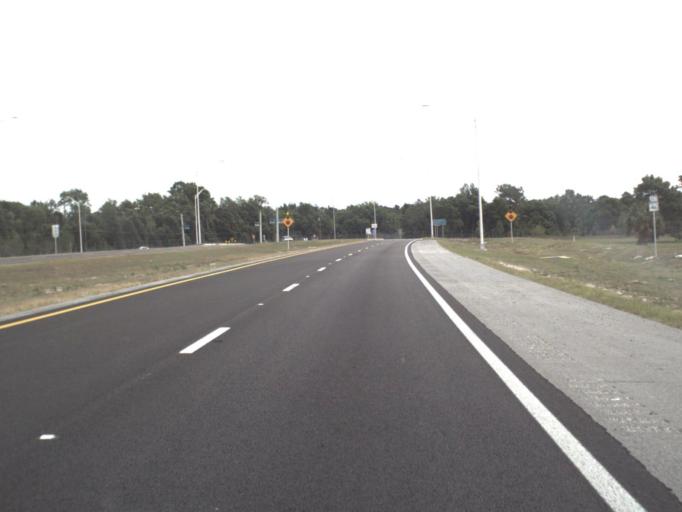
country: US
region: Florida
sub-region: Lake County
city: Mount Plymouth
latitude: 28.8111
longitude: -81.5068
